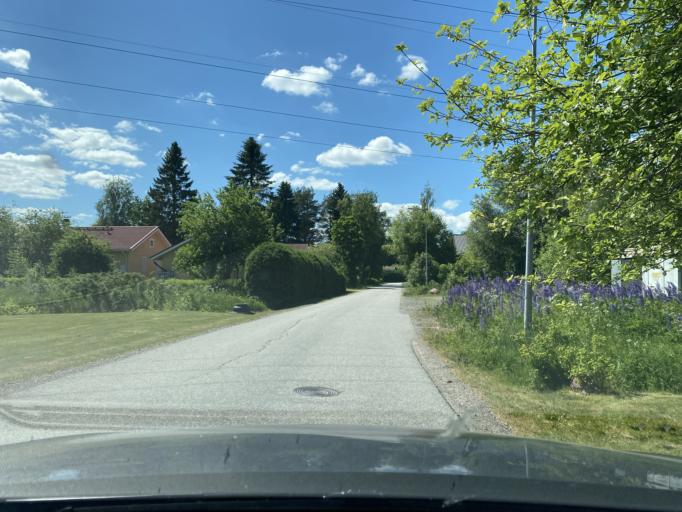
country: FI
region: Satakunta
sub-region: Rauma
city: Eura
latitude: 61.1141
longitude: 22.1424
